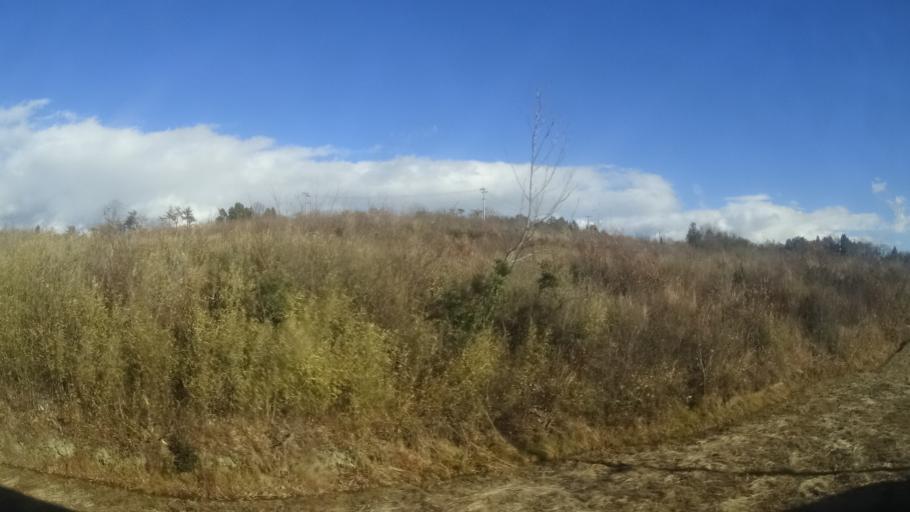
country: JP
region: Miyagi
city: Marumori
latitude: 37.8586
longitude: 140.9298
